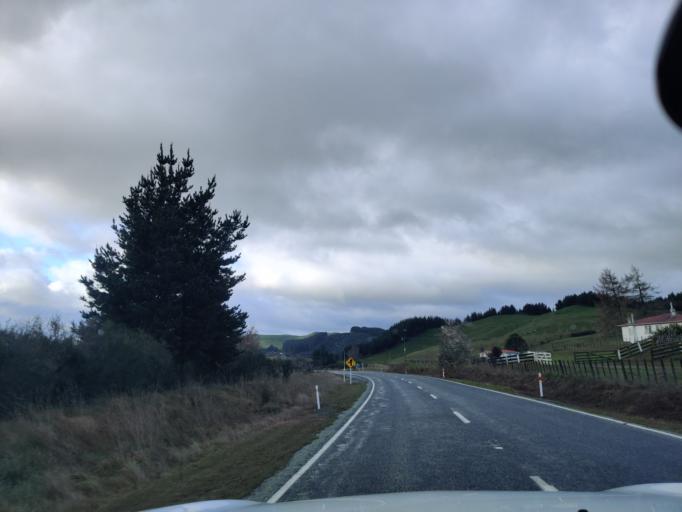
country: NZ
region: Waikato
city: Turangi
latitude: -38.8617
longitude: 175.6822
